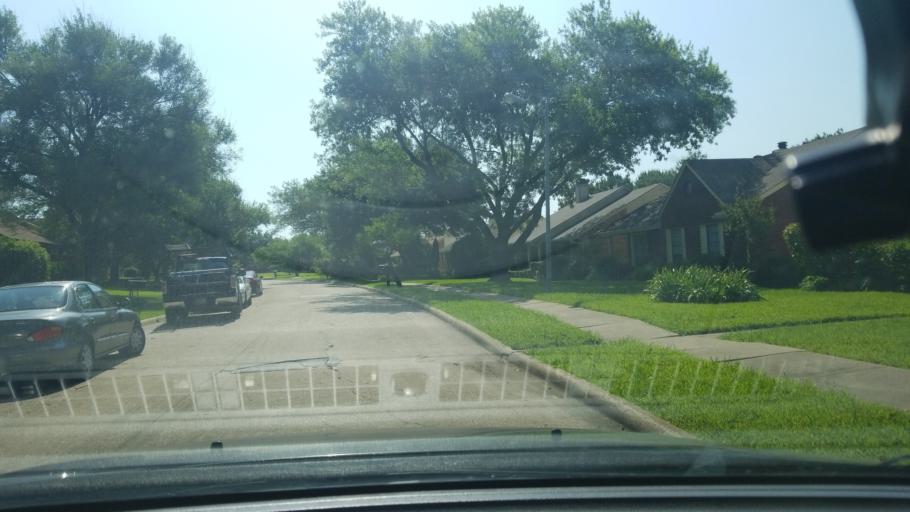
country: US
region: Texas
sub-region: Dallas County
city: Mesquite
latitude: 32.8174
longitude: -96.6249
